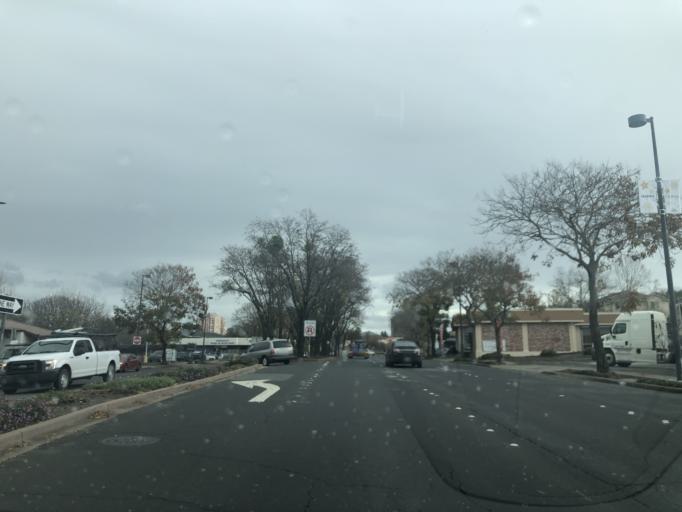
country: US
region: California
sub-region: Contra Costa County
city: Concord
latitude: 37.9785
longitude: -122.0409
